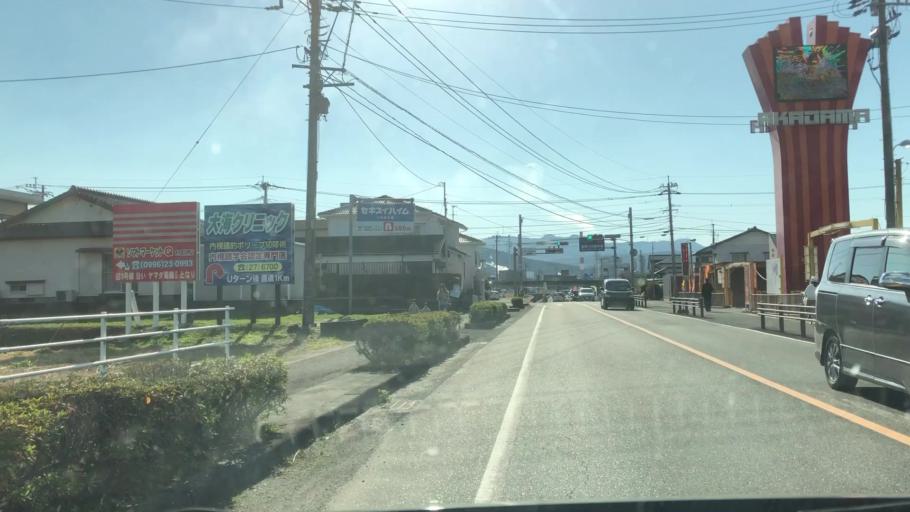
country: JP
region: Kagoshima
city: Satsumasendai
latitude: 31.8292
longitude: 130.3059
